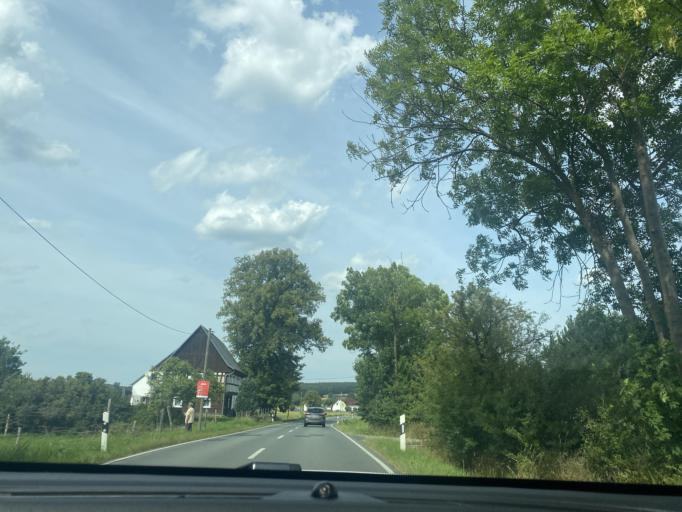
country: DE
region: Saxony
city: Grosshennersdorf
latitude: 50.9952
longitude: 14.7921
